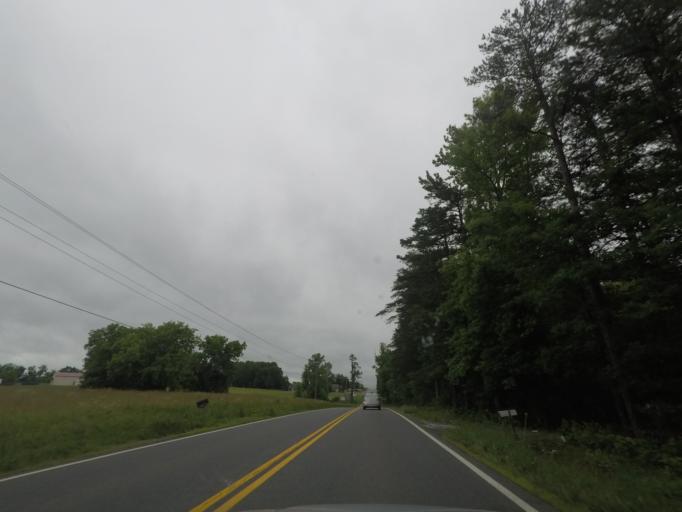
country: US
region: Virginia
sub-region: Fluvanna County
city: Palmyra
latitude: 37.9644
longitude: -78.2251
